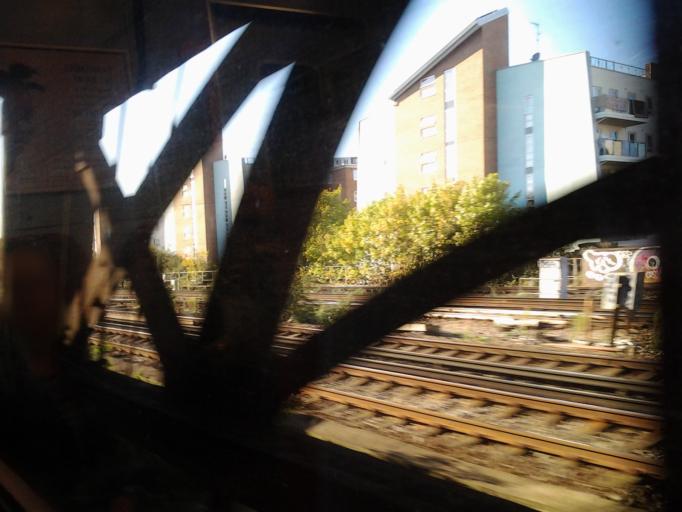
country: GB
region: England
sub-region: Greater London
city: Battersea
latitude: 51.4740
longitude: -0.1488
